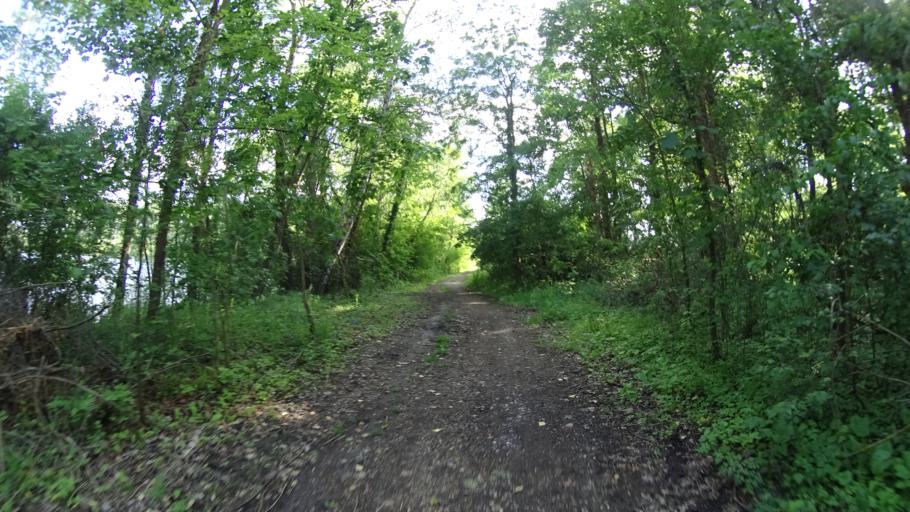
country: DE
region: Baden-Wuerttemberg
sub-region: Karlsruhe Region
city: Eggenstein-Leopoldshafen
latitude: 49.0669
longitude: 8.3467
